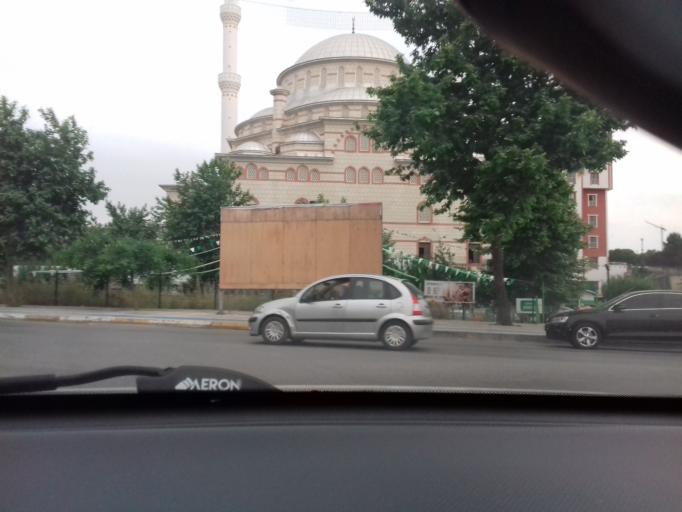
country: TR
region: Istanbul
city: Sultanbeyli
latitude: 40.9313
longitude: 29.3044
